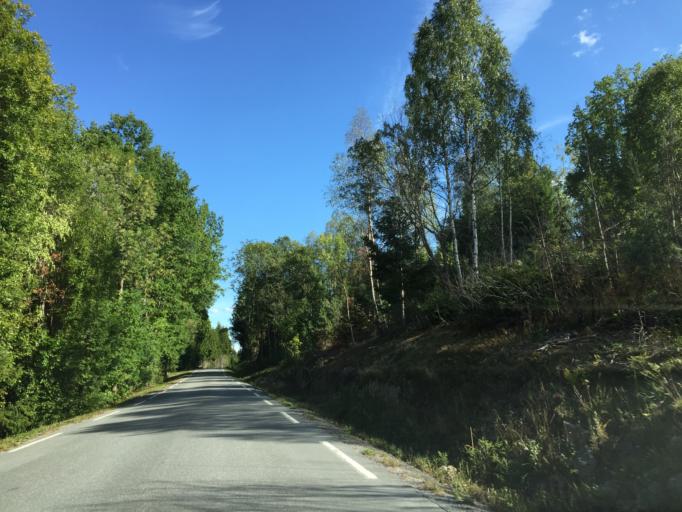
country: NO
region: Buskerud
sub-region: Ovre Eiker
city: Hokksund
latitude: 59.6605
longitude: 9.9003
